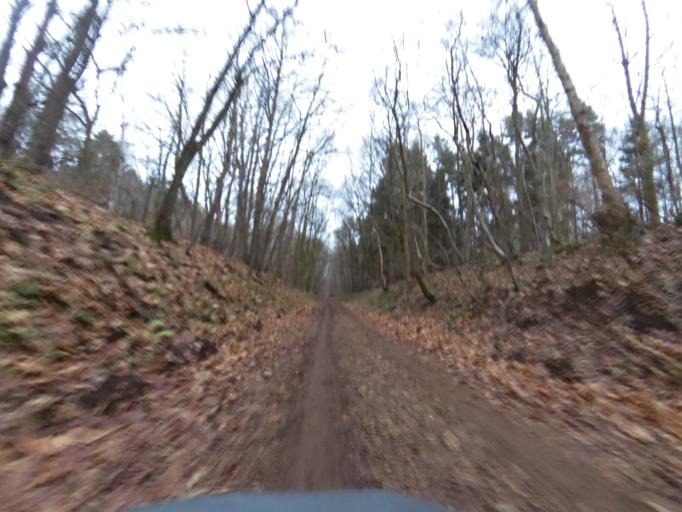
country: GB
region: England
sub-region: Norfolk
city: Costessey
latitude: 52.7070
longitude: 1.1805
